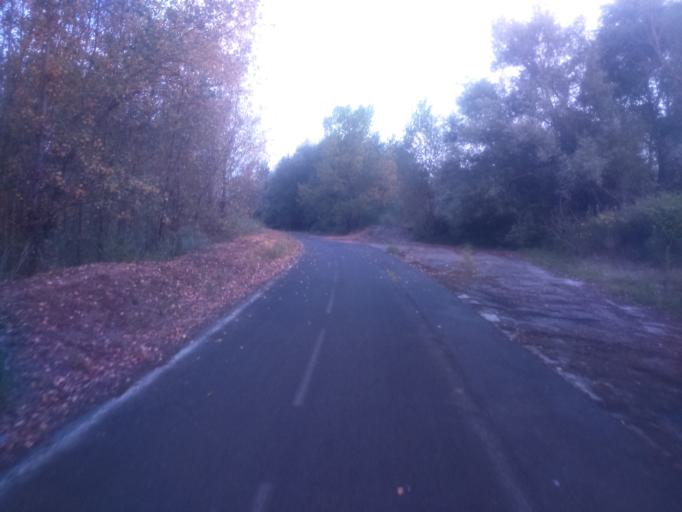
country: FR
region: Aquitaine
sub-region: Departement de la Gironde
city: Le Bouscat
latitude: 44.8859
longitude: -0.5588
